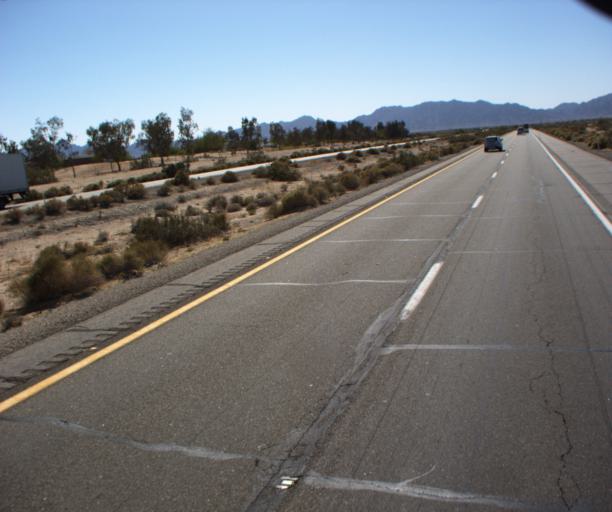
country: US
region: Arizona
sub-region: Yuma County
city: Wellton
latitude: 32.6531
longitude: -114.1800
